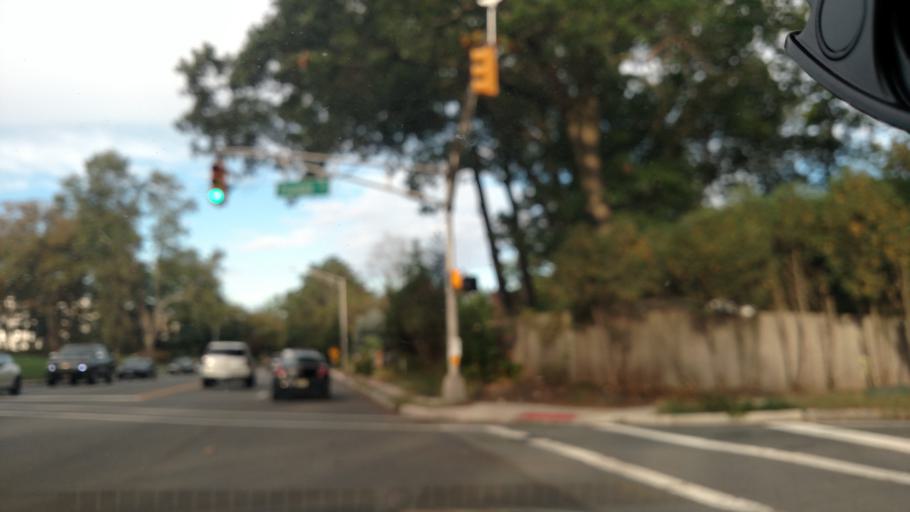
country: US
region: New Jersey
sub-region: Morris County
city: Morristown
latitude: 40.7888
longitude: -74.4602
